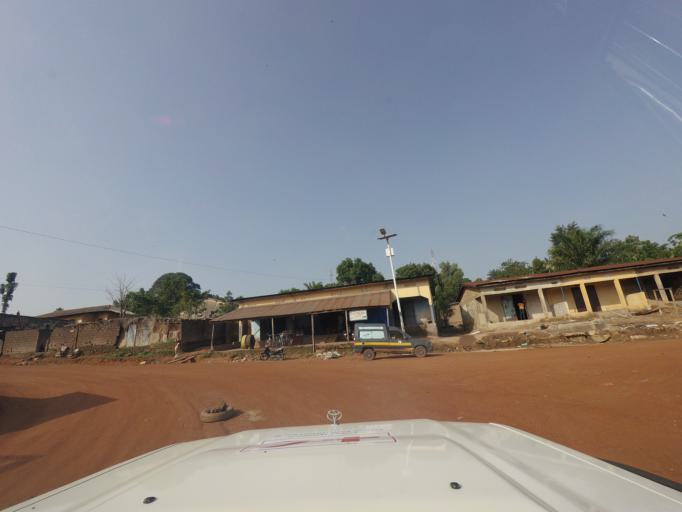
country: GN
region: Nzerekore
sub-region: Prefecture de Guekedou
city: Gueckedou
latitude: 8.5620
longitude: -10.1355
